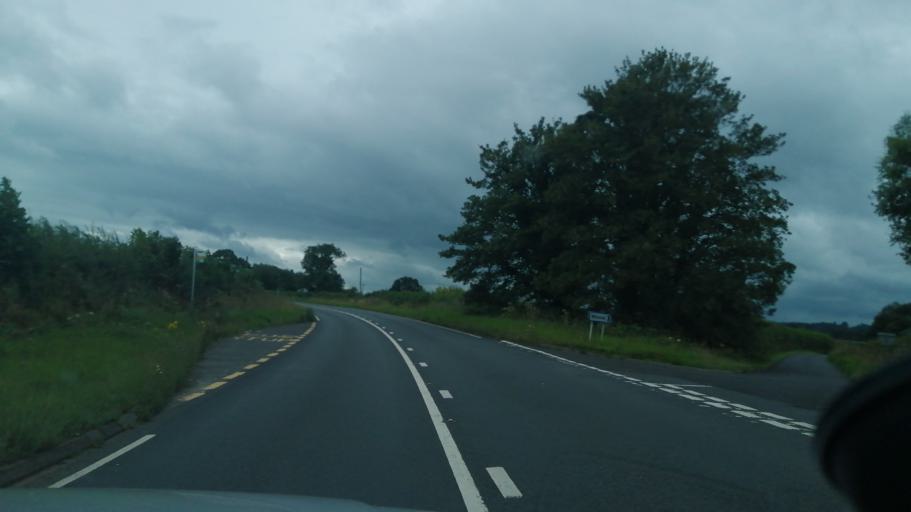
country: GB
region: England
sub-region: Herefordshire
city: Thruxton
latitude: 52.0087
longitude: -2.7908
